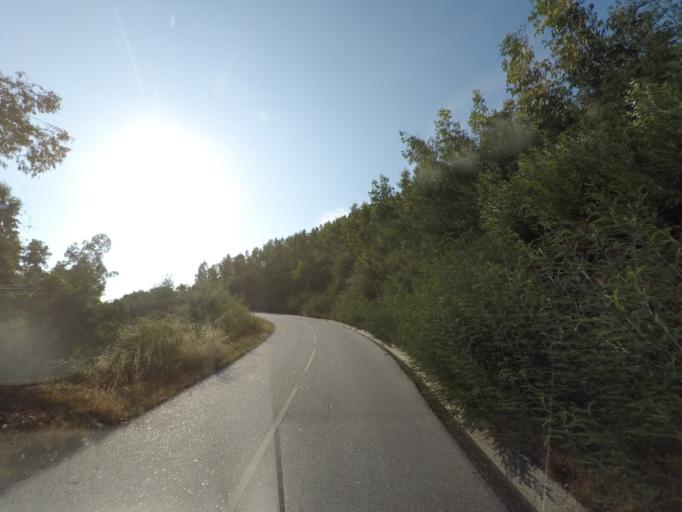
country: PT
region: Vila Real
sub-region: Mesao Frio
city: Mesao Frio
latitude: 41.1640
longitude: -7.9134
